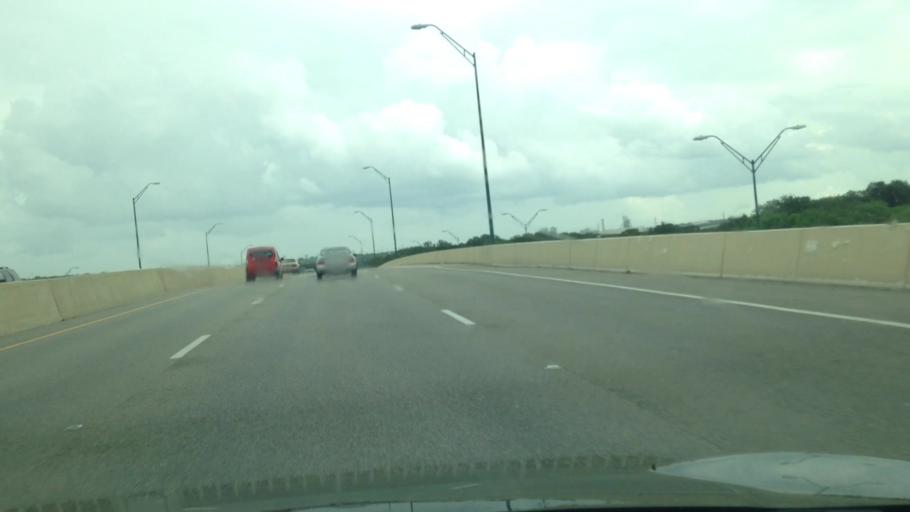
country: US
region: Texas
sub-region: Bexar County
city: Alamo Heights
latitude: 29.5452
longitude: -98.4551
